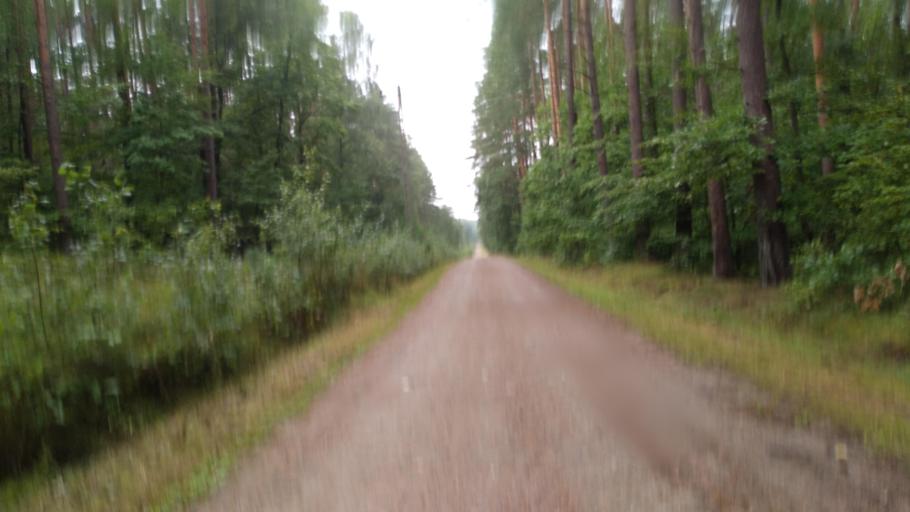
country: PL
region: Pomeranian Voivodeship
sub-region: Powiat wejherowski
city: Goscicino
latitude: 54.6191
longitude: 18.1552
